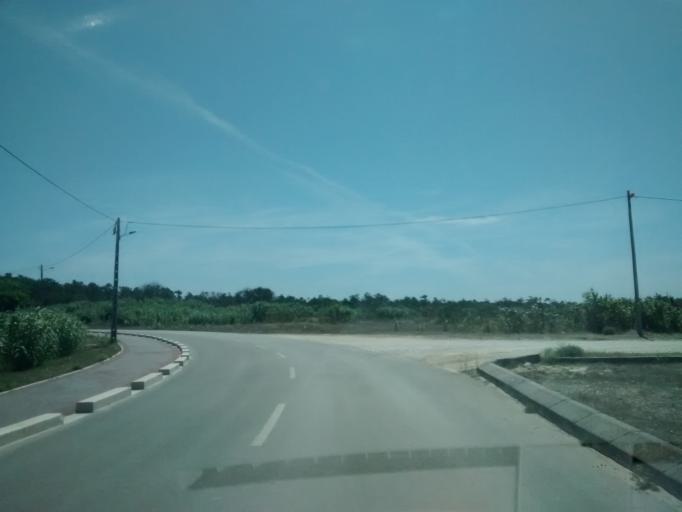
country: PT
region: Coimbra
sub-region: Mira
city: Mira
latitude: 40.4456
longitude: -8.8038
